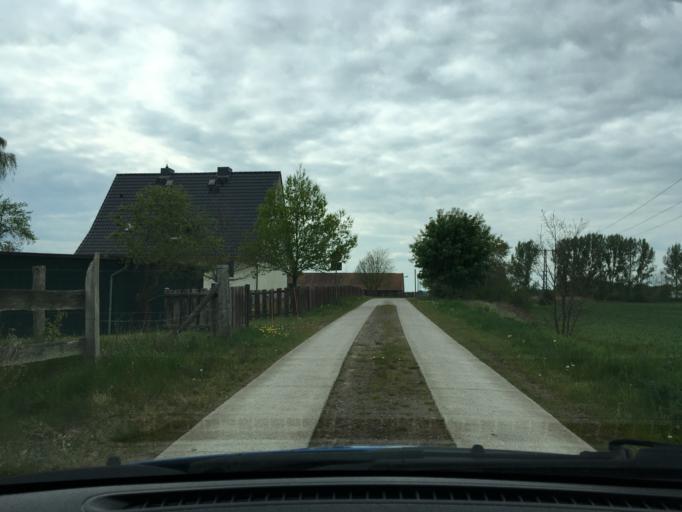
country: DE
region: Lower Saxony
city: Neu Darchau
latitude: 53.2808
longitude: 10.9185
